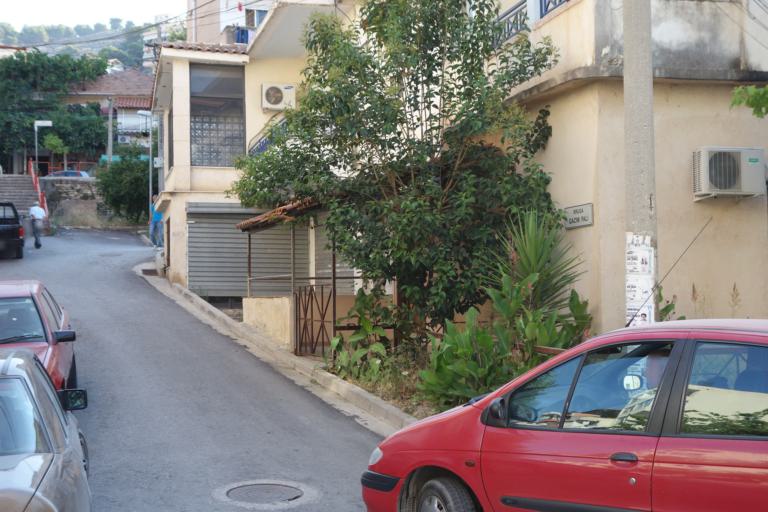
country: AL
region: Vlore
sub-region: Rrethi i Sarandes
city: Sarande
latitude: 39.8747
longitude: 20.0103
